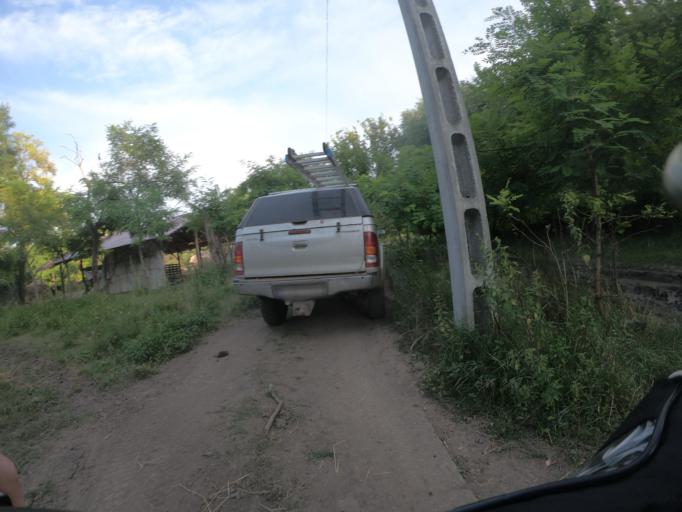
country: HU
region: Borsod-Abauj-Zemplen
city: Mezokeresztes
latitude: 47.7678
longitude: 20.7873
